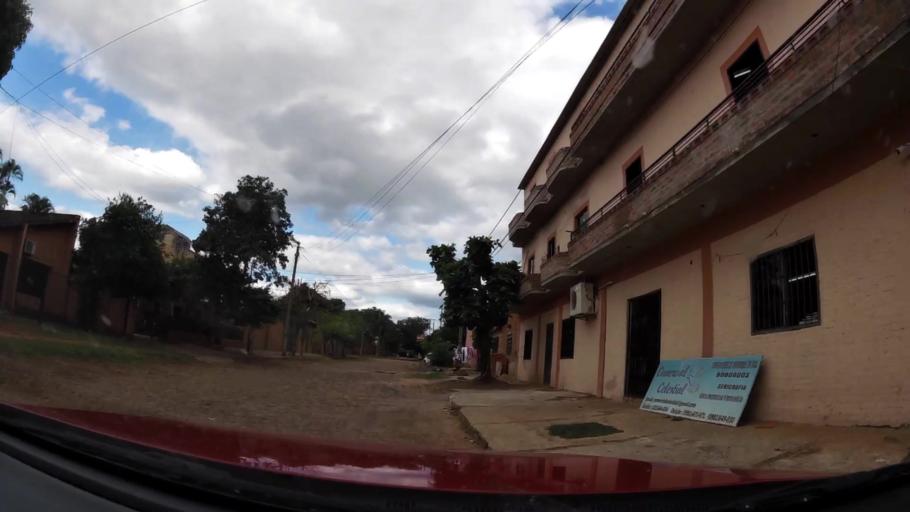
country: PY
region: Central
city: San Lorenzo
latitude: -25.2726
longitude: -57.5051
